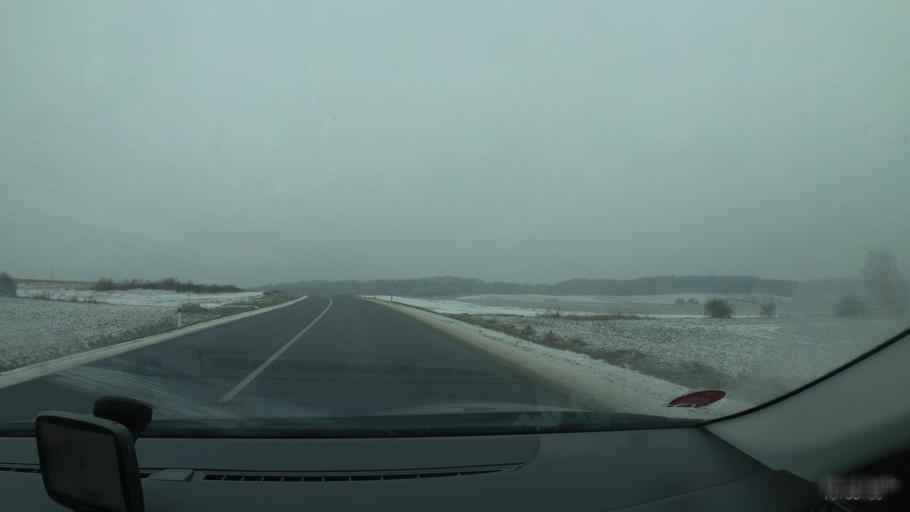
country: CZ
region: Central Bohemia
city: Revnicov
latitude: 50.1817
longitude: 13.8163
